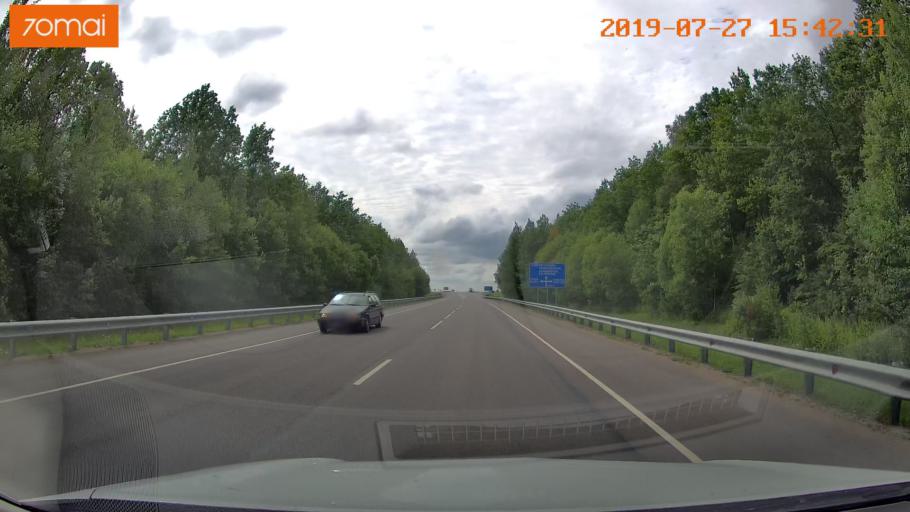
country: RU
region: Kaliningrad
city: Gusev
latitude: 54.6175
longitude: 22.2147
